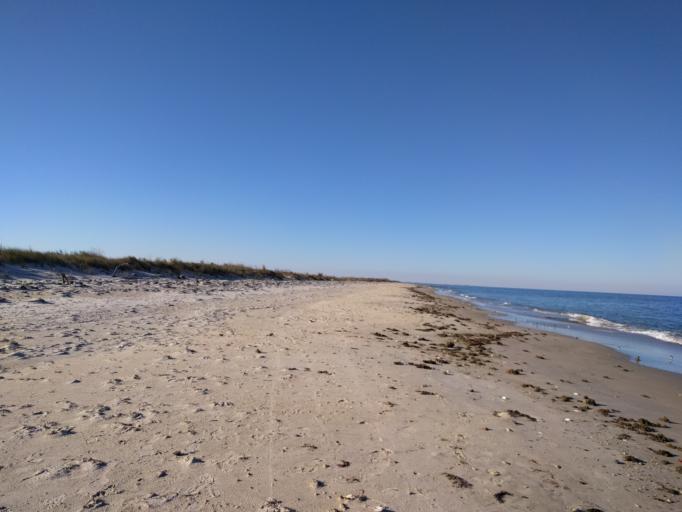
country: US
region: Virginia
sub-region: City of Poquoson
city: Poquoson
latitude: 37.0972
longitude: -76.2767
